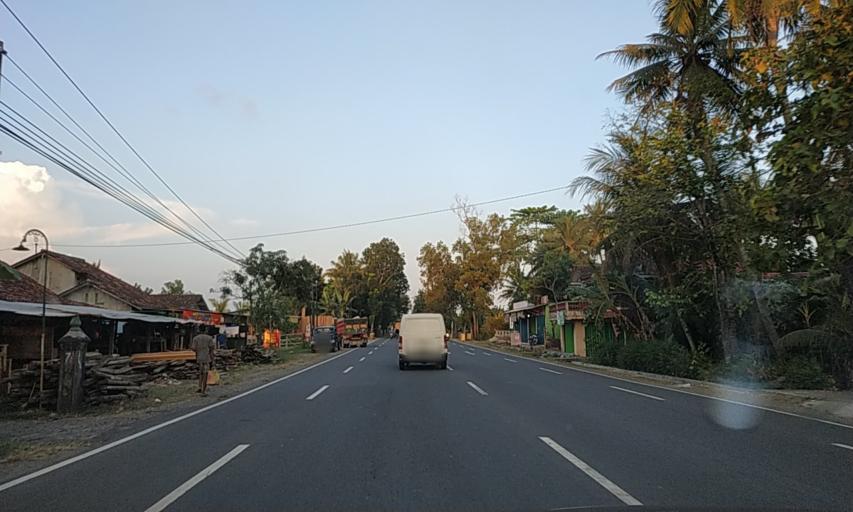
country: ID
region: Daerah Istimewa Yogyakarta
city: Srandakan
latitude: -7.8875
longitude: 110.0893
